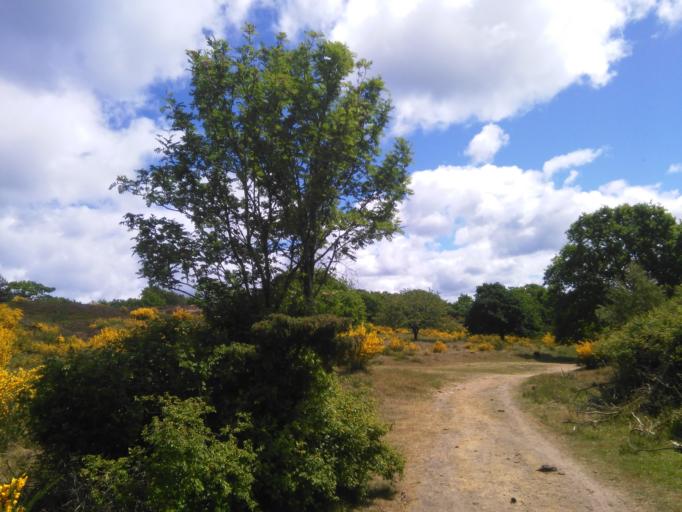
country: DK
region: Capital Region
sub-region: Bornholm Kommune
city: Ronne
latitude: 55.2934
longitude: 14.7726
